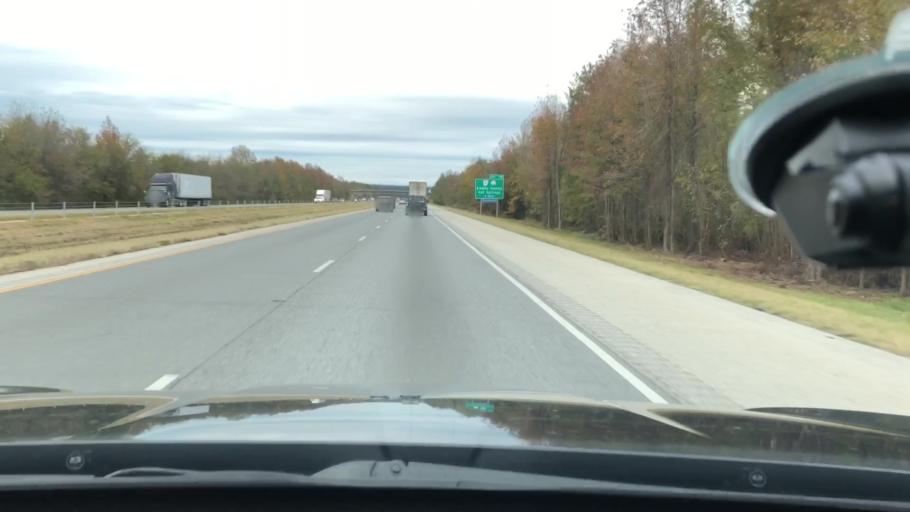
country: US
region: Arkansas
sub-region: Clark County
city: Arkadelphia
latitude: 34.1668
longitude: -93.0757
